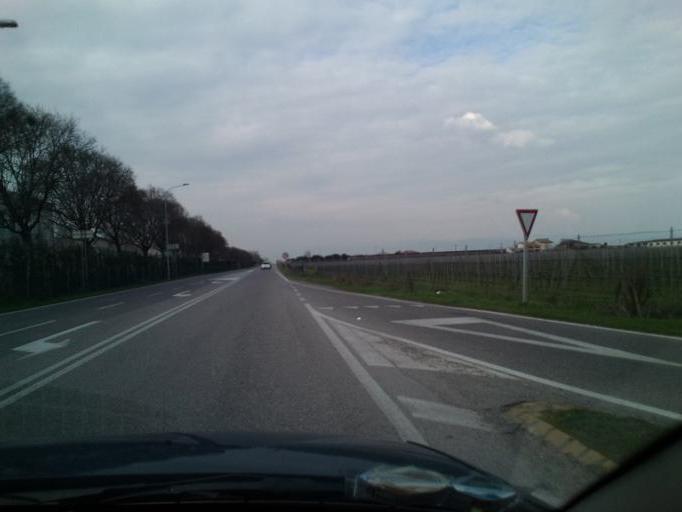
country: IT
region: Veneto
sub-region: Provincia di Verona
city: Sommacampagna
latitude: 45.4018
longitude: 10.8511
